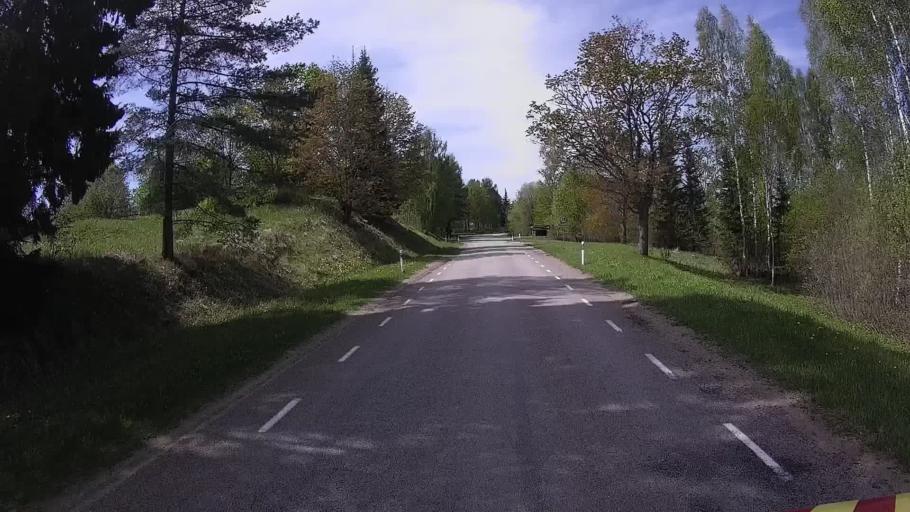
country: EE
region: Valgamaa
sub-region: Valga linn
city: Valga
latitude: 57.6462
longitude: 26.3175
